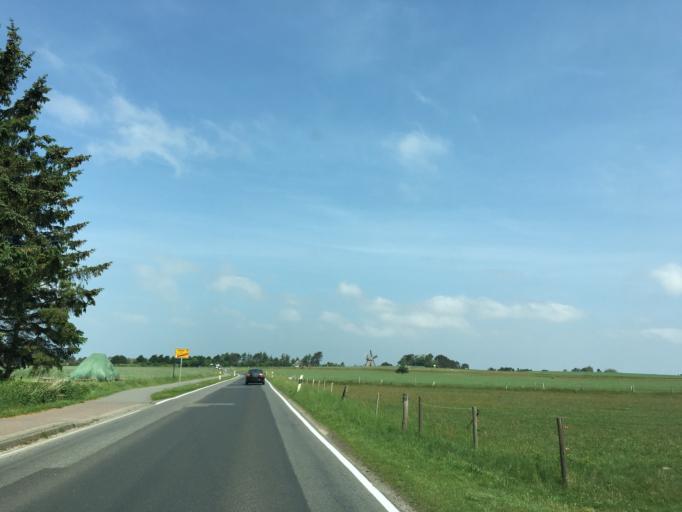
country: DE
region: Schleswig-Holstein
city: Nebel
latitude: 54.6436
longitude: 8.3550
